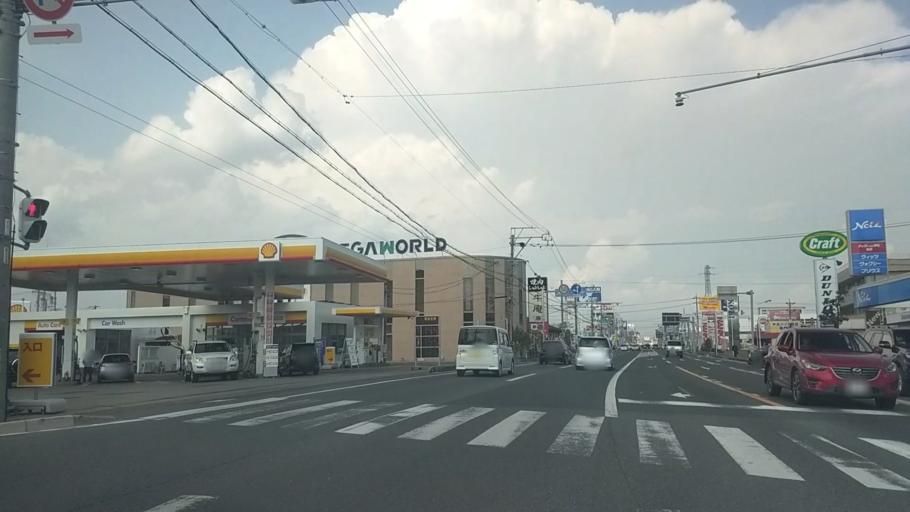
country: JP
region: Shizuoka
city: Hamamatsu
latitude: 34.7210
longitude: 137.7650
